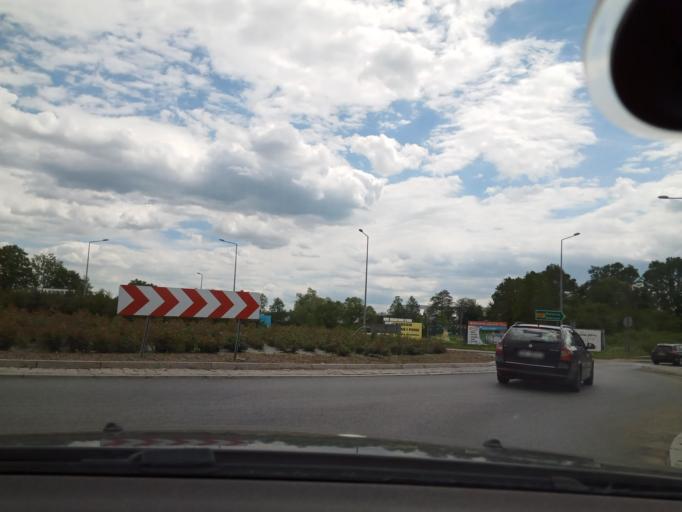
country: PL
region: Lesser Poland Voivodeship
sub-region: Powiat wielicki
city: Gdow
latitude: 49.9148
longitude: 20.1936
